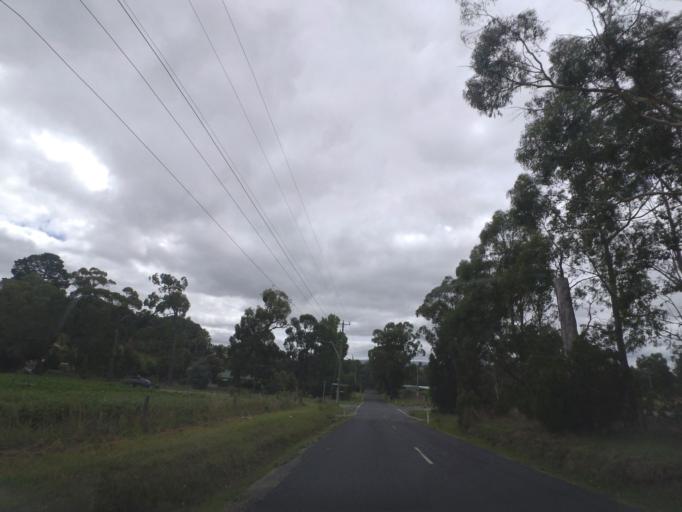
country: AU
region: Victoria
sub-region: Yarra Ranges
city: Mount Evelyn
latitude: -37.7952
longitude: 145.4563
